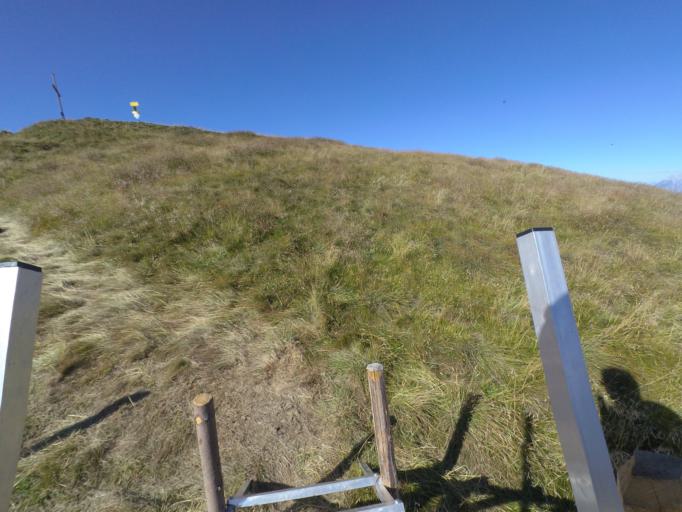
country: AT
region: Salzburg
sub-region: Politischer Bezirk Sankt Johann im Pongau
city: Goldegg
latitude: 47.3658
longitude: 13.0696
